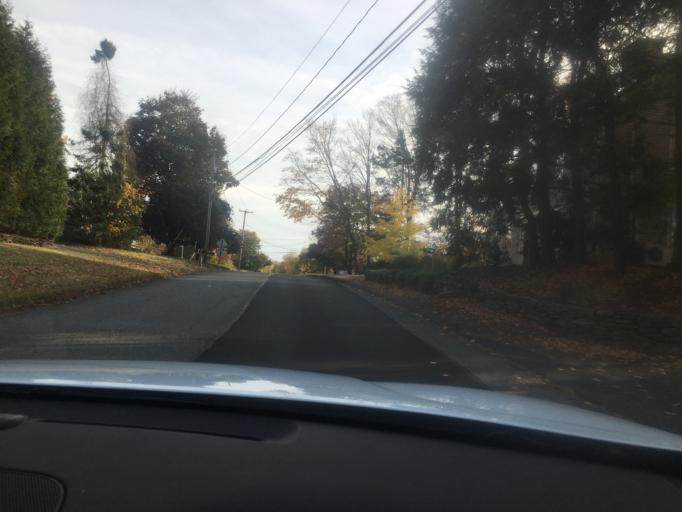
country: US
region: Connecticut
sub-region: Hartford County
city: Broad Brook
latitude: 41.8775
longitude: -72.5751
